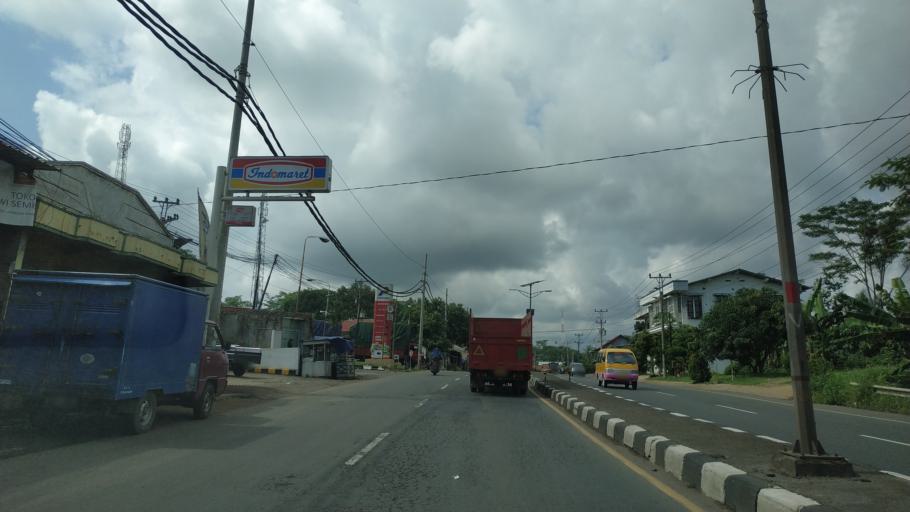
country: ID
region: Central Java
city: Pekalongan
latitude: -6.9345
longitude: 109.7732
